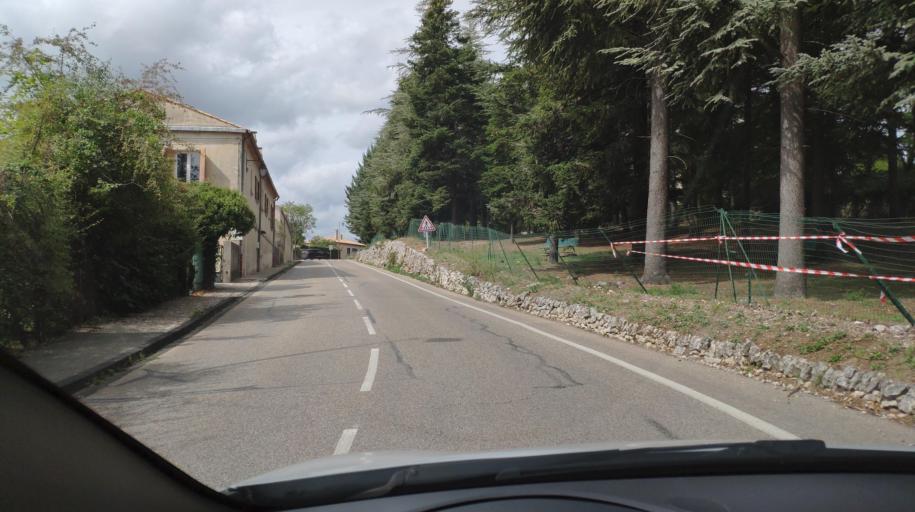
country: FR
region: Provence-Alpes-Cote d'Azur
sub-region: Departement du Vaucluse
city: Sault
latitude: 44.0937
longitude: 5.4121
